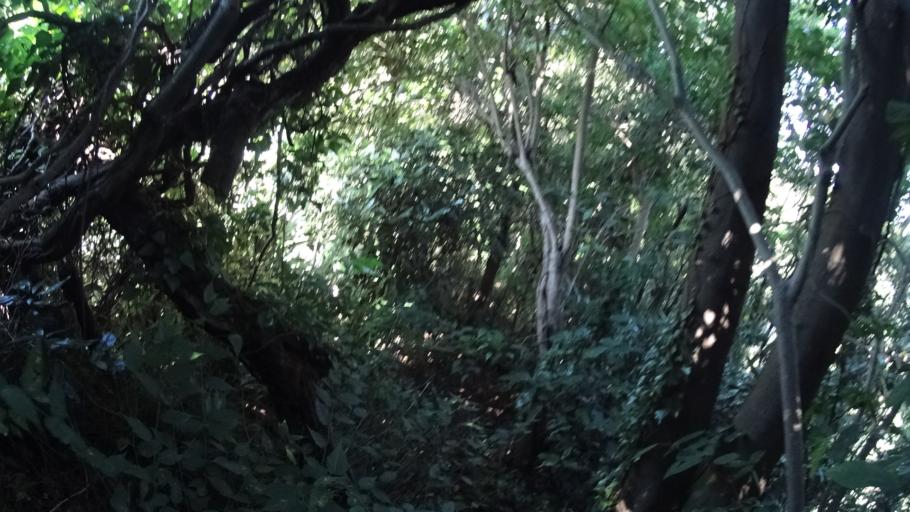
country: JP
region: Kanagawa
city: Hayama
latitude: 35.2774
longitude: 139.6082
